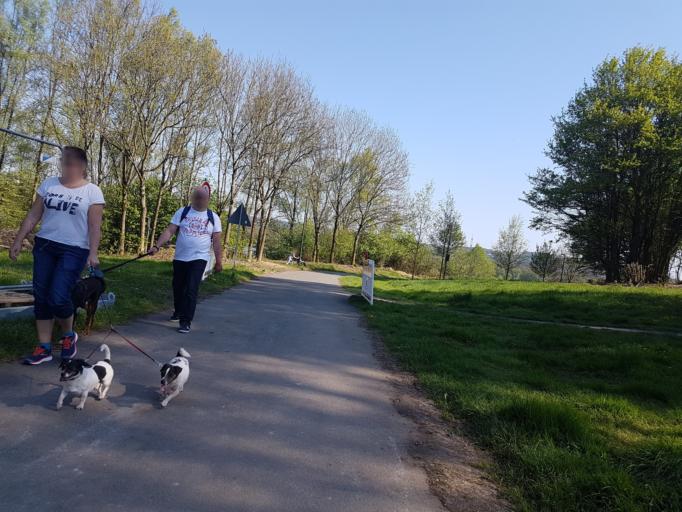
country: DE
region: North Rhine-Westphalia
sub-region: Regierungsbezirk Arnsberg
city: Bochum
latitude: 51.4207
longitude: 7.2550
